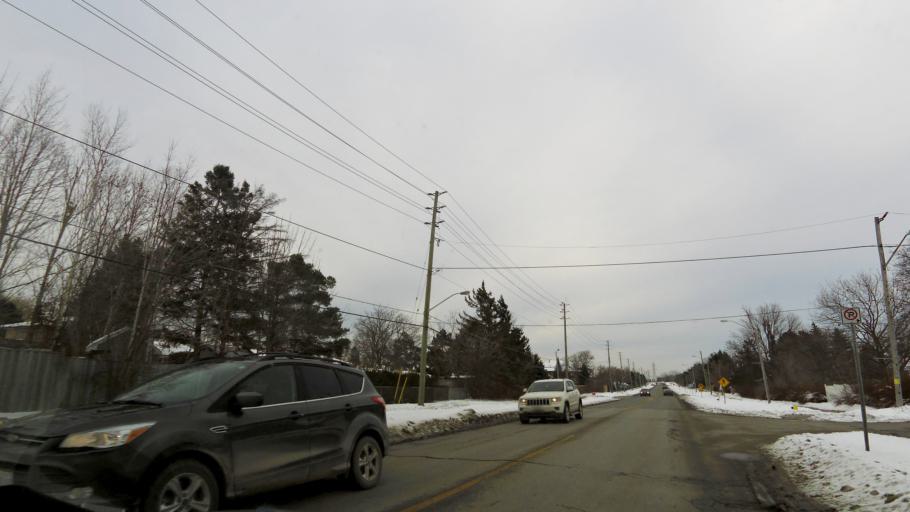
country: CA
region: Ontario
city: Vaughan
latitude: 43.8399
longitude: -79.6246
